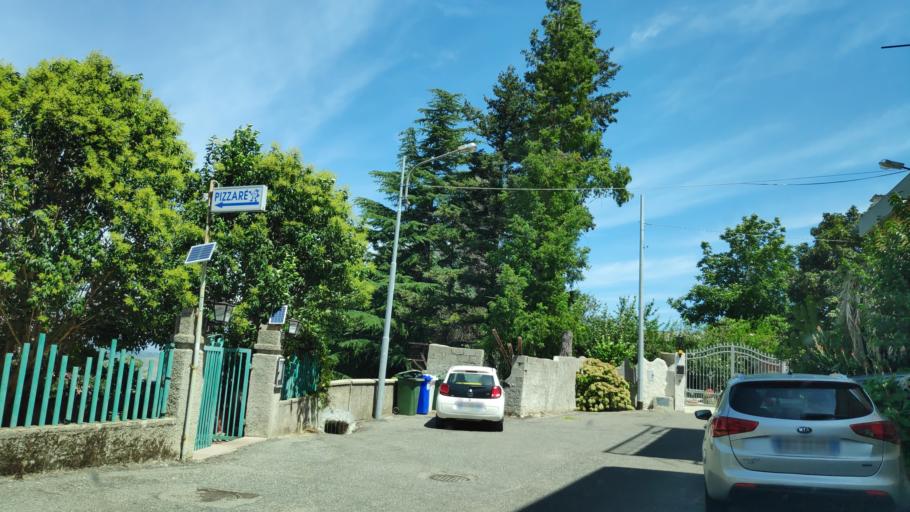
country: IT
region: Calabria
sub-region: Provincia di Catanzaro
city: Palermiti
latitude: 38.7491
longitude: 16.4546
